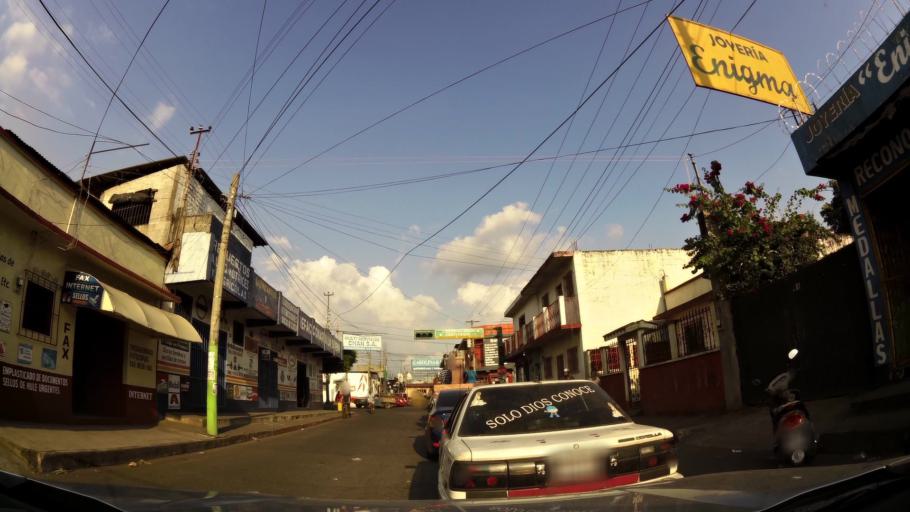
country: GT
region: Retalhuleu
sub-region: Municipio de Retalhuleu
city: Retalhuleu
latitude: 14.5346
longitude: -91.6827
